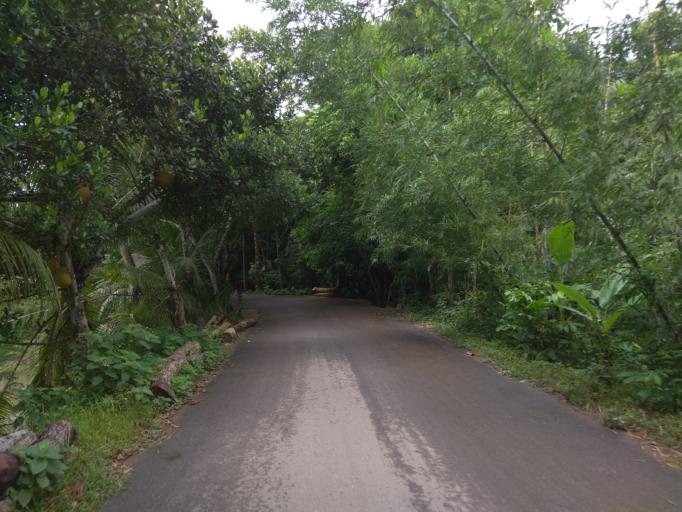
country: BD
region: Dhaka
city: Dohar
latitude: 23.4220
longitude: 90.0648
